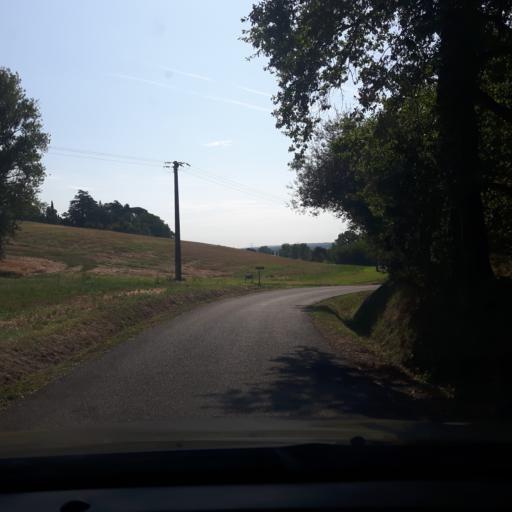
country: FR
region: Midi-Pyrenees
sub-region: Departement de la Haute-Garonne
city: Bouloc
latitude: 43.7711
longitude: 1.4100
